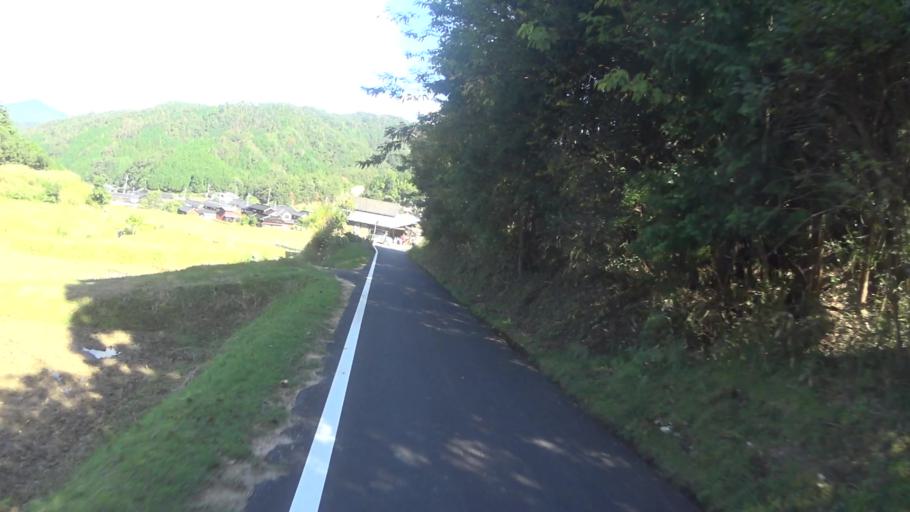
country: JP
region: Hyogo
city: Toyooka
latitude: 35.5446
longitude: 134.9755
